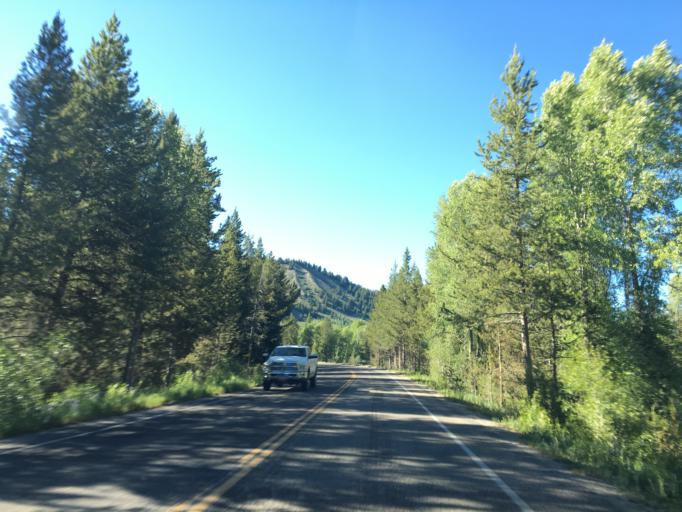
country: US
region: Wyoming
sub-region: Teton County
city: Jackson
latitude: 43.8512
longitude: -110.5178
